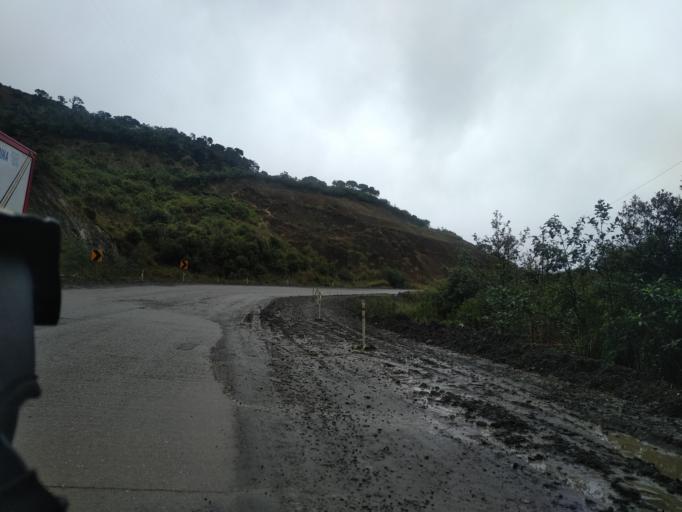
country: EC
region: Loja
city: Catamayo
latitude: -3.8650
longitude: -79.2792
